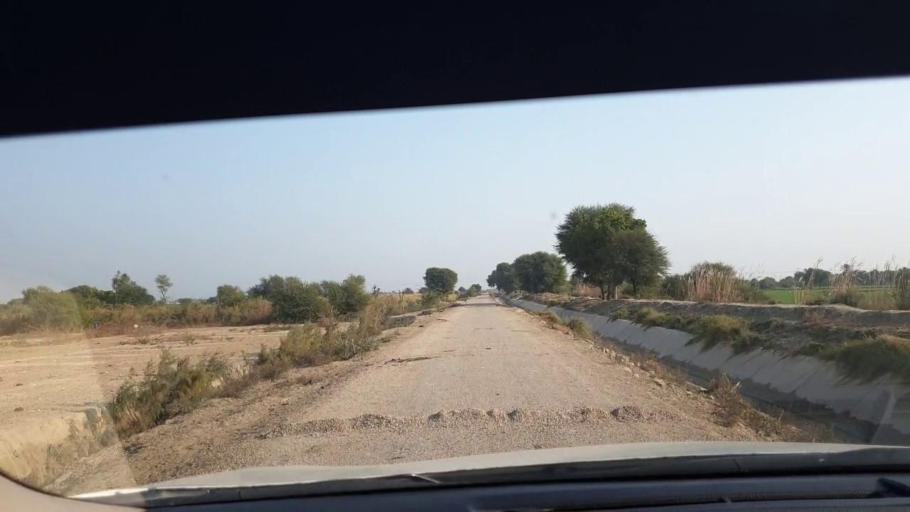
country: PK
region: Sindh
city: Berani
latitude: 25.8339
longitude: 68.7738
